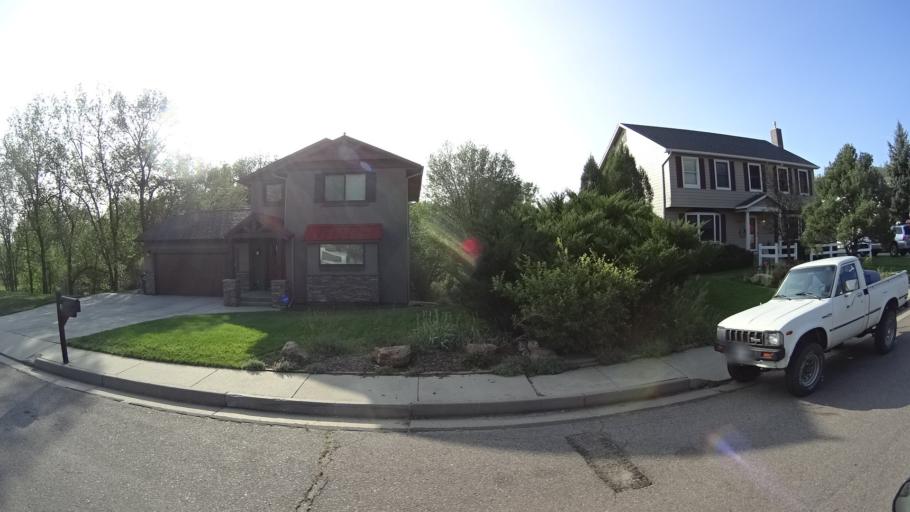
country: US
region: Colorado
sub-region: El Paso County
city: Colorado Springs
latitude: 38.8157
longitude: -104.8505
